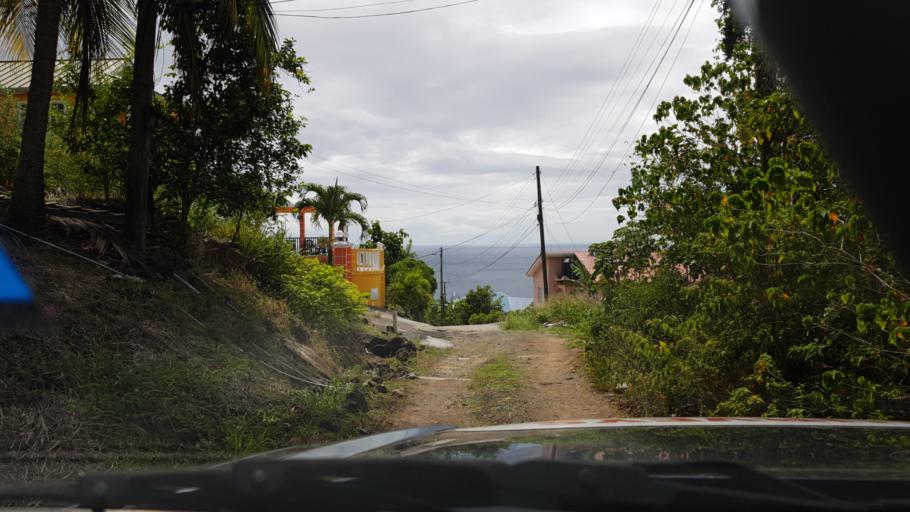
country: LC
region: Anse-la-Raye
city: Anse La Raye
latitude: 13.9463
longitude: -61.0368
